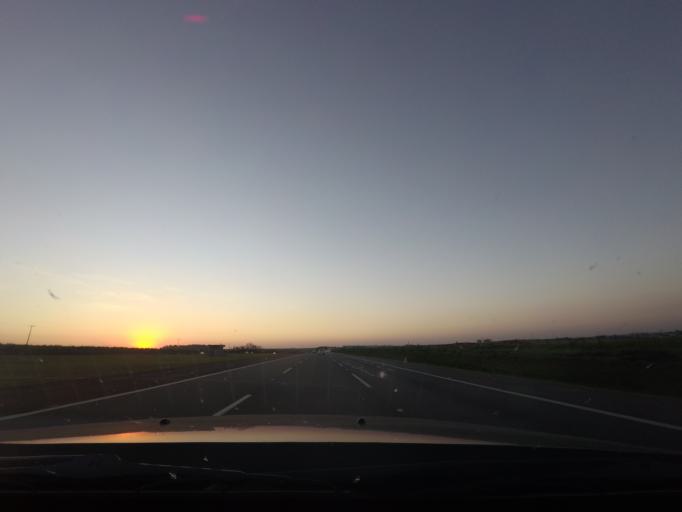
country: BR
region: Sao Paulo
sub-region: Santa Barbara D'Oeste
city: Santa Barbara d'Oeste
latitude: -22.7875
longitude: -47.4230
